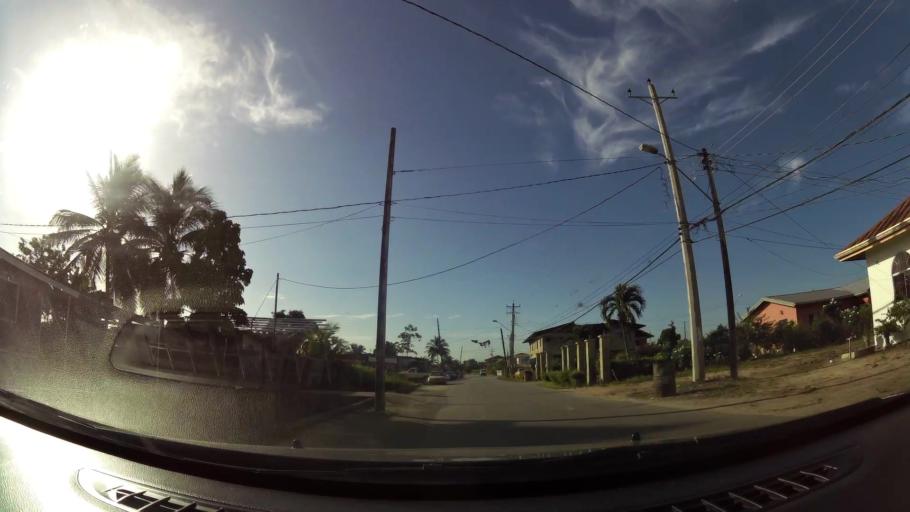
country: TT
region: Chaguanas
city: Chaguanas
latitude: 10.5683
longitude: -61.3799
